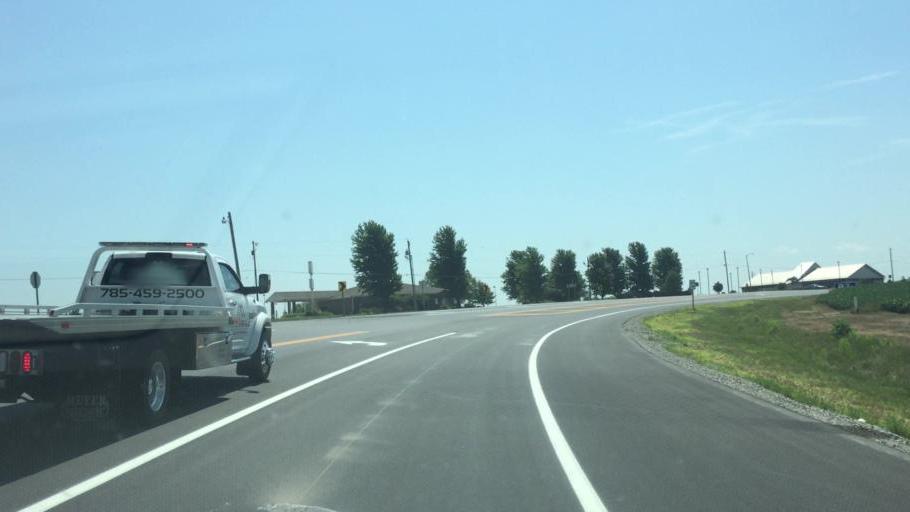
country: US
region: Kansas
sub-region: Brown County
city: Hiawatha
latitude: 39.8479
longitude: -95.5661
